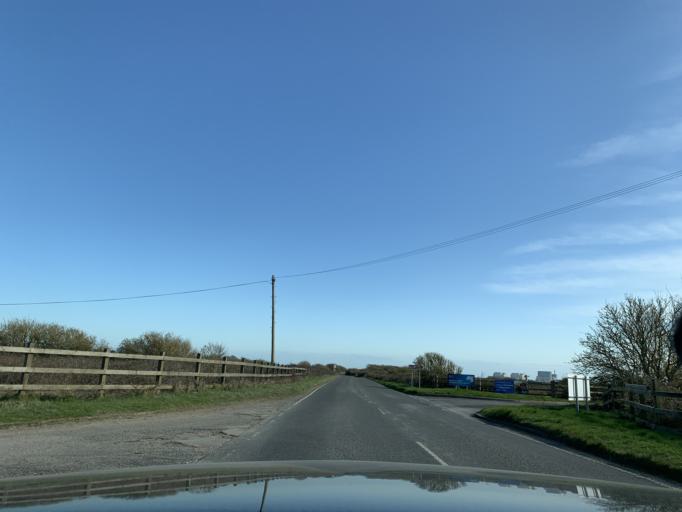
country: GB
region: England
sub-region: Kent
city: Lydd
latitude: 50.9396
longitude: 0.9342
